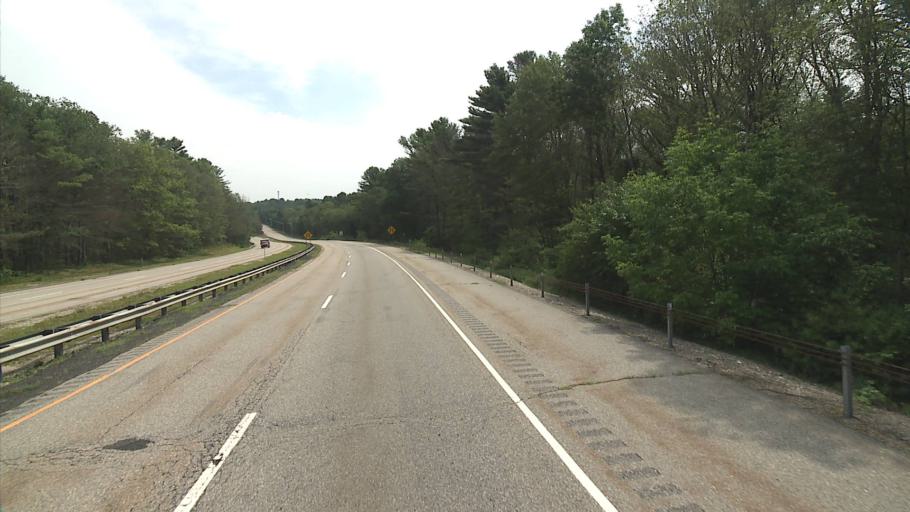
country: US
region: Rhode Island
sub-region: Providence County
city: Foster
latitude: 41.7888
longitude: -71.8027
